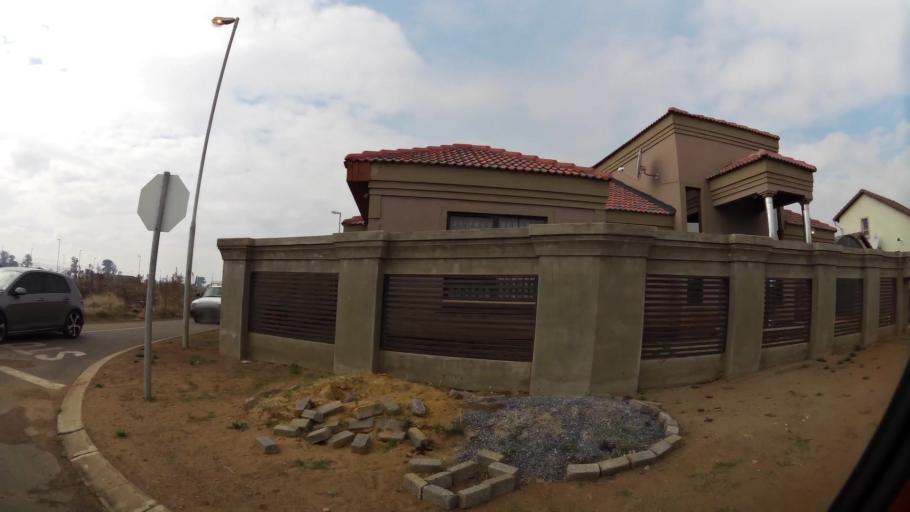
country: ZA
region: Gauteng
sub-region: Sedibeng District Municipality
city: Vanderbijlpark
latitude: -26.6855
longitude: 27.8514
